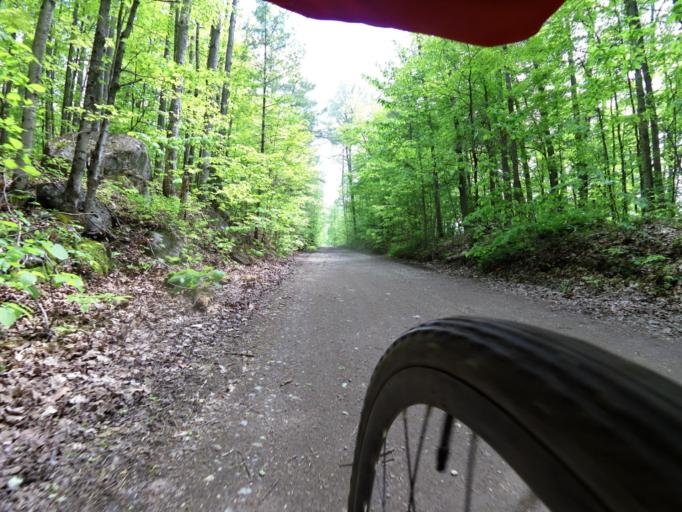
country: CA
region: Ontario
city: Renfrew
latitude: 45.1985
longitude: -76.6850
